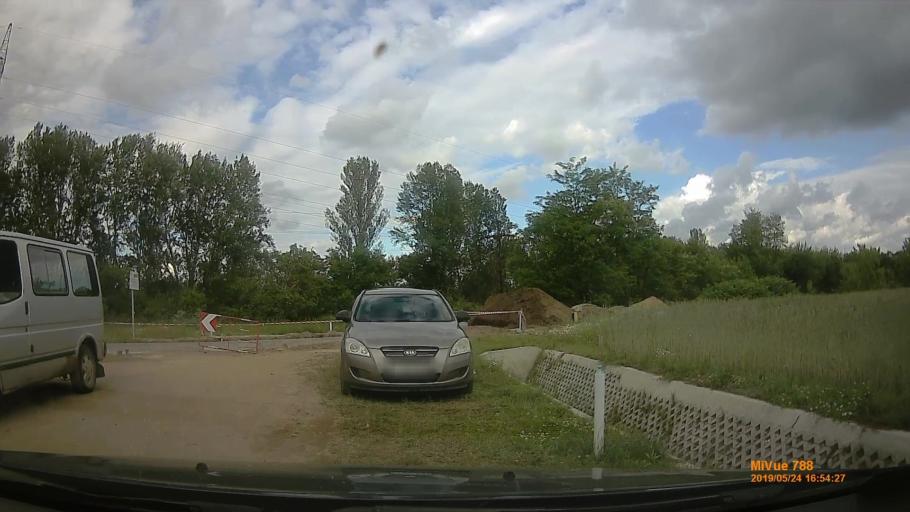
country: HU
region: Budapest
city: Budapest XVII. keruelet
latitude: 47.5111
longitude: 19.2310
